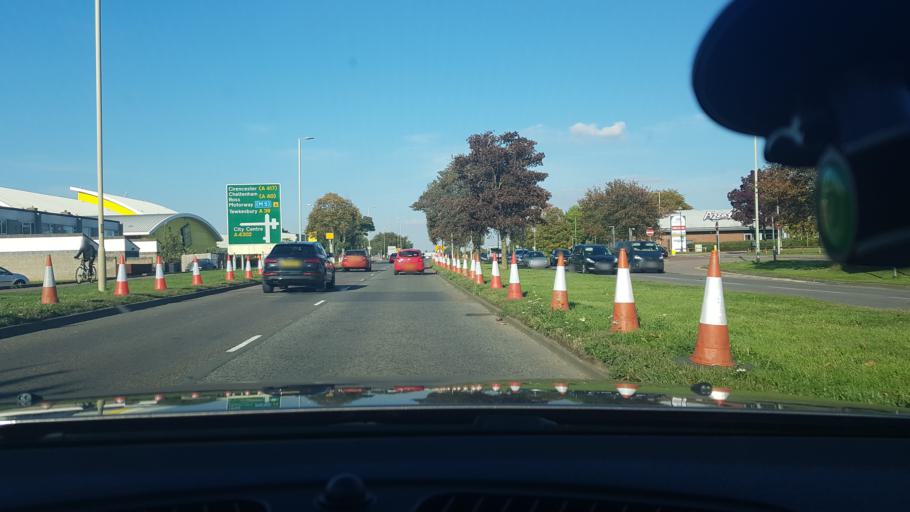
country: GB
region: England
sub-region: Gloucestershire
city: Gloucester
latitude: 51.8553
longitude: -2.2233
